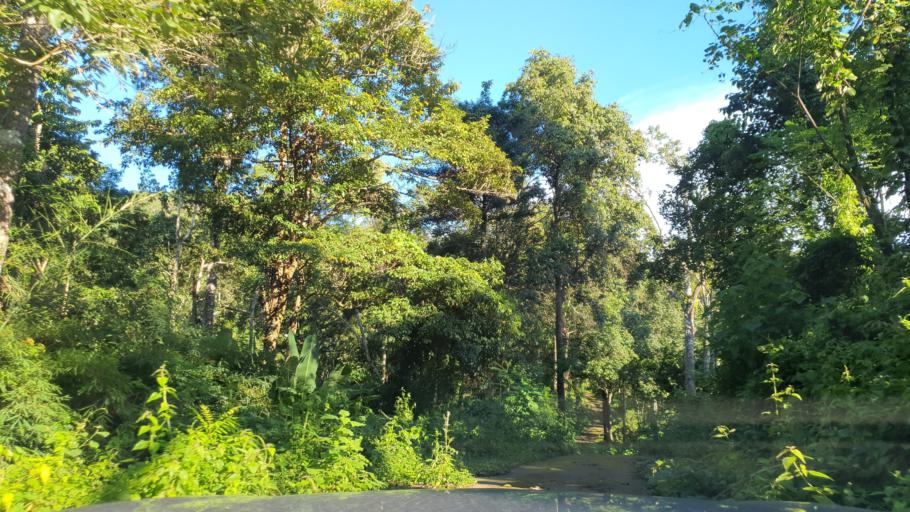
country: TH
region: Chiang Mai
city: Mae On
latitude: 18.8146
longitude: 99.3531
